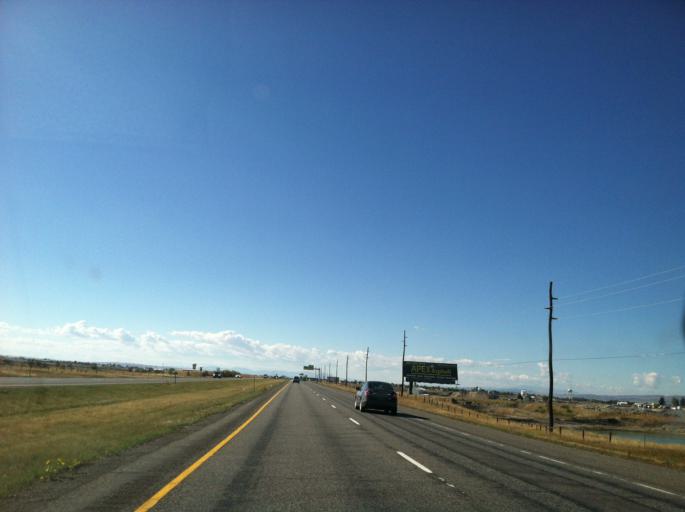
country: US
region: Montana
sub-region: Gallatin County
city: Belgrade
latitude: 45.7546
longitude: -111.1461
